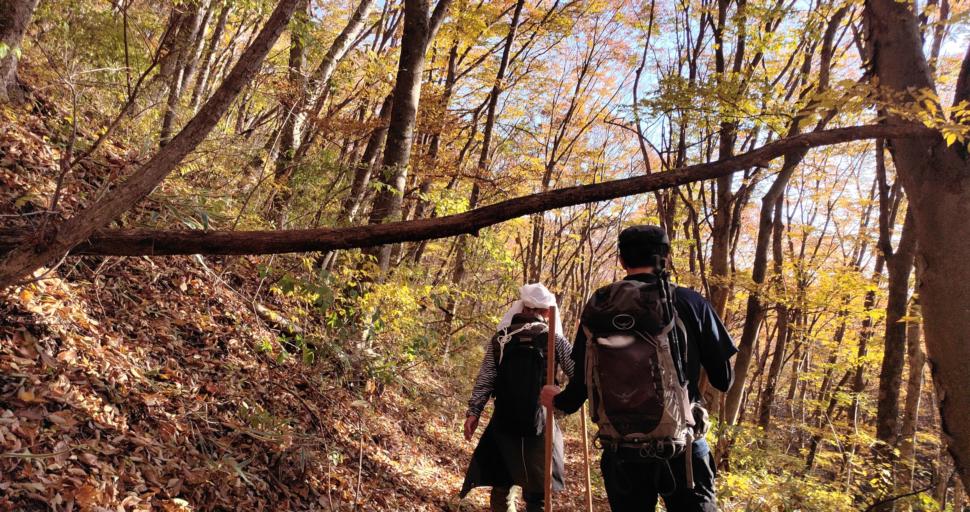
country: JP
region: Nagano
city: Komoro
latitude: 36.3877
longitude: 138.4384
